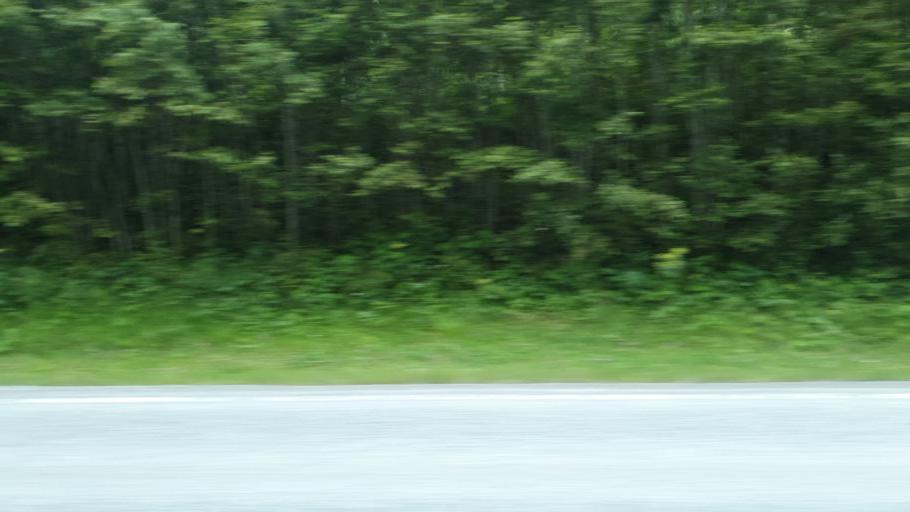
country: NO
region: Sor-Trondelag
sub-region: Midtre Gauldal
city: Storen
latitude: 63.0023
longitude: 10.2379
